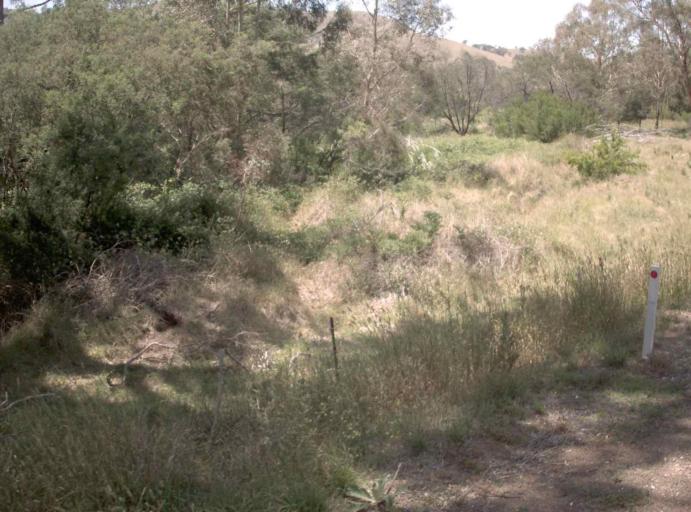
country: AU
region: Victoria
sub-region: East Gippsland
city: Bairnsdale
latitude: -37.2223
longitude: 147.7155
